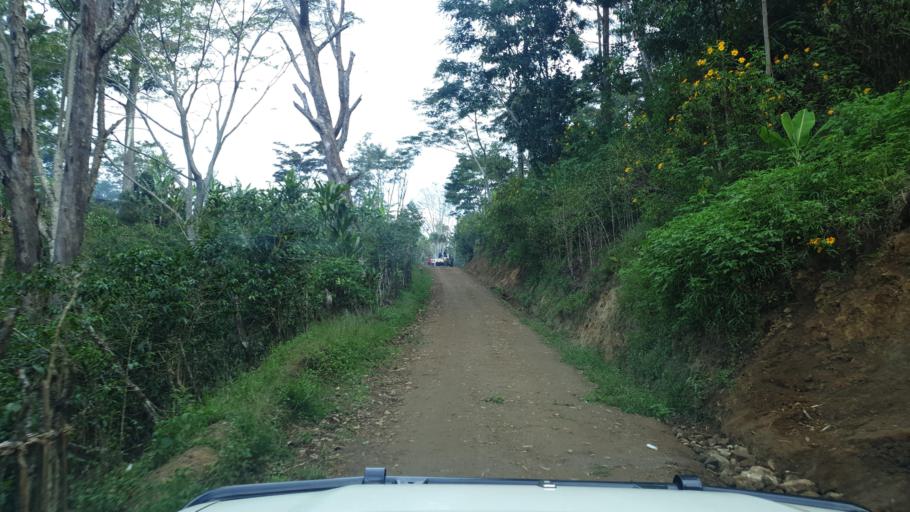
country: PG
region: Eastern Highlands
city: Goroka
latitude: -5.9412
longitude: 145.2701
